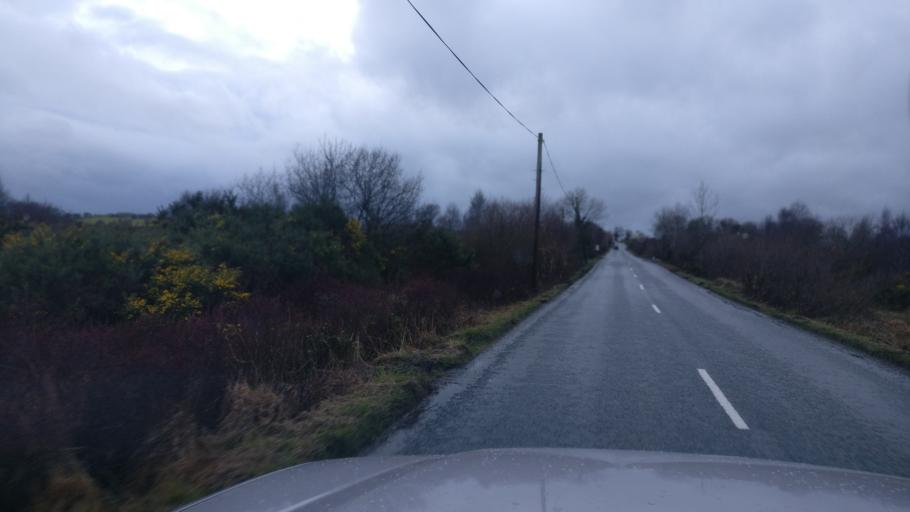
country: IE
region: Leinster
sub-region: An Iarmhi
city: Athlone
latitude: 53.4182
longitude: -8.0678
